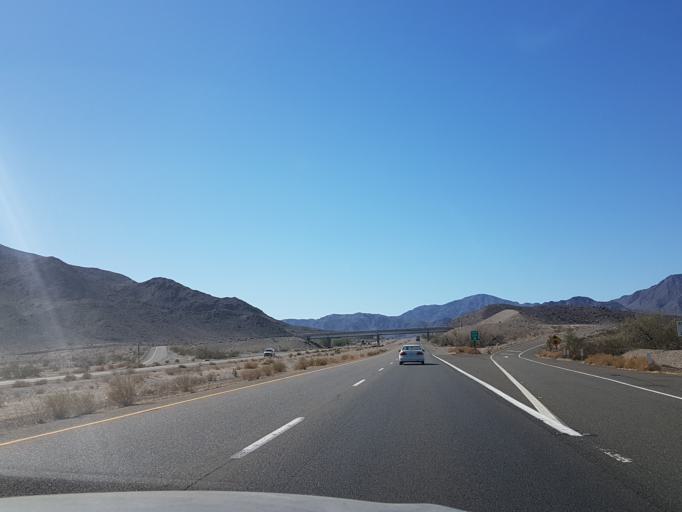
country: US
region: California
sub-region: San Bernardino County
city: Fort Irwin
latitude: 35.1963
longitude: -116.1370
